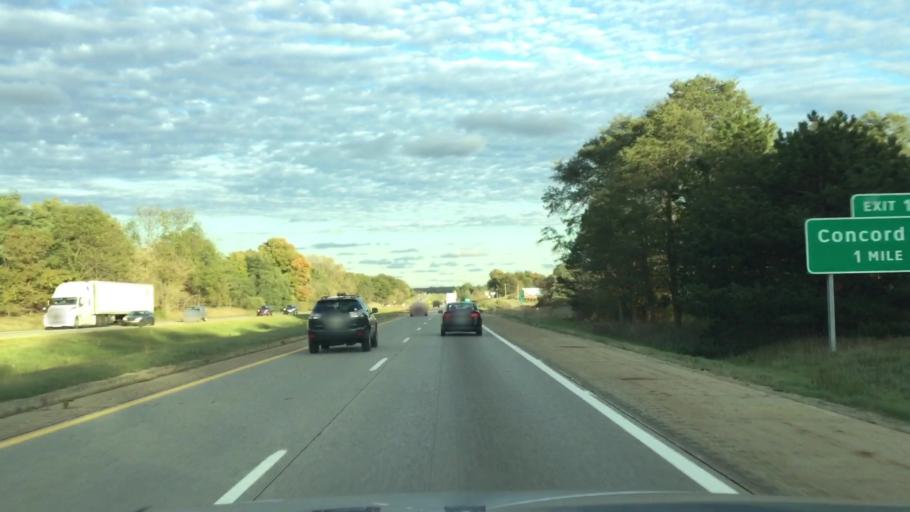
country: US
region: Michigan
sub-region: Calhoun County
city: Albion
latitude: 42.2620
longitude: -84.6676
